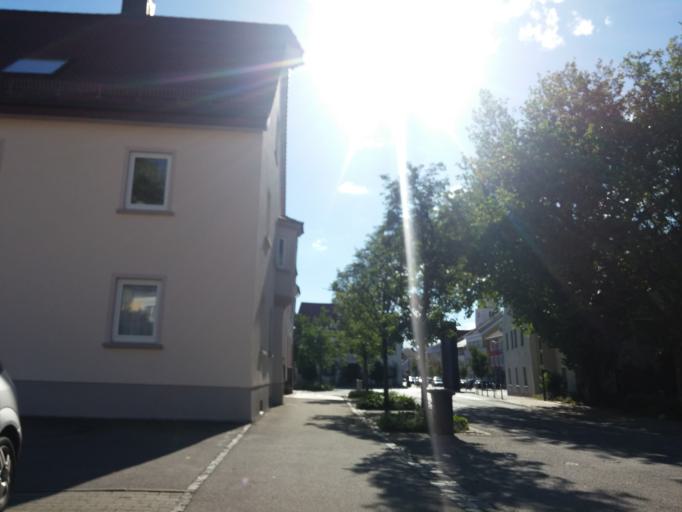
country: DE
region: Bavaria
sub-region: Swabia
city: Illertissen
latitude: 48.2230
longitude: 10.1089
